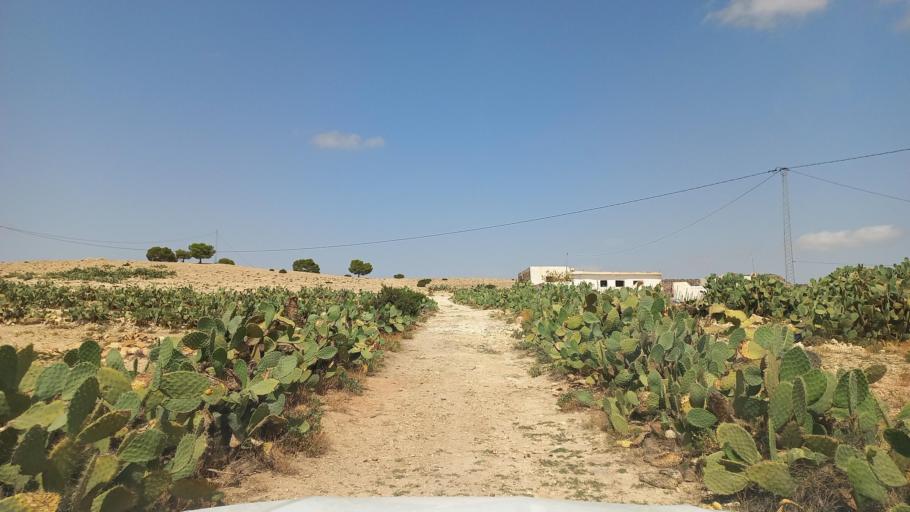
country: TN
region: Al Qasrayn
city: Sbiba
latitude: 35.4024
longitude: 8.9689
